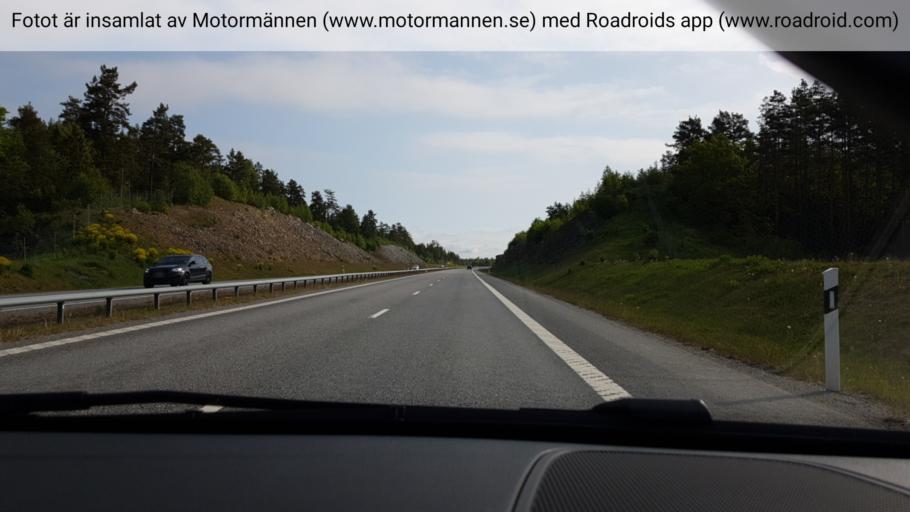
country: SE
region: Stockholm
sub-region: Nynashamns Kommun
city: Osmo
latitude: 59.0407
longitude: 17.9701
